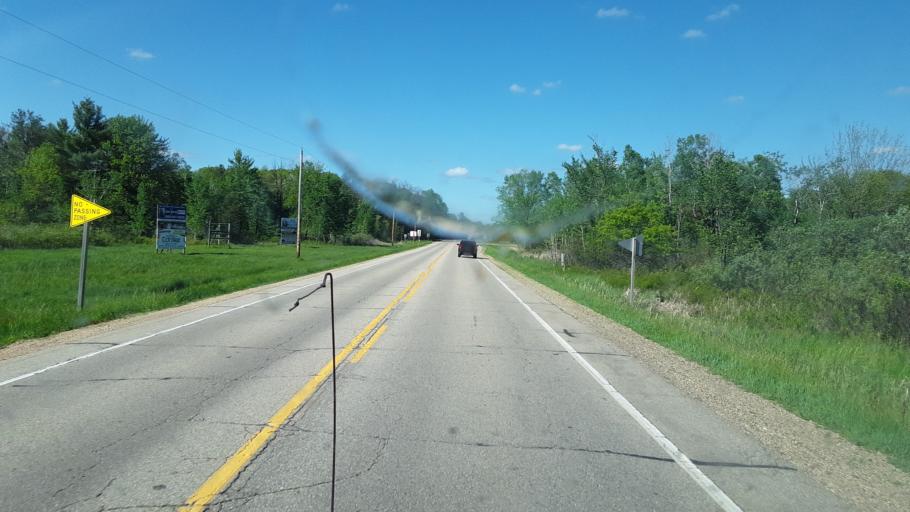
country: US
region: Wisconsin
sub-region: Juneau County
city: New Lisbon
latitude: 43.9065
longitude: -90.1299
